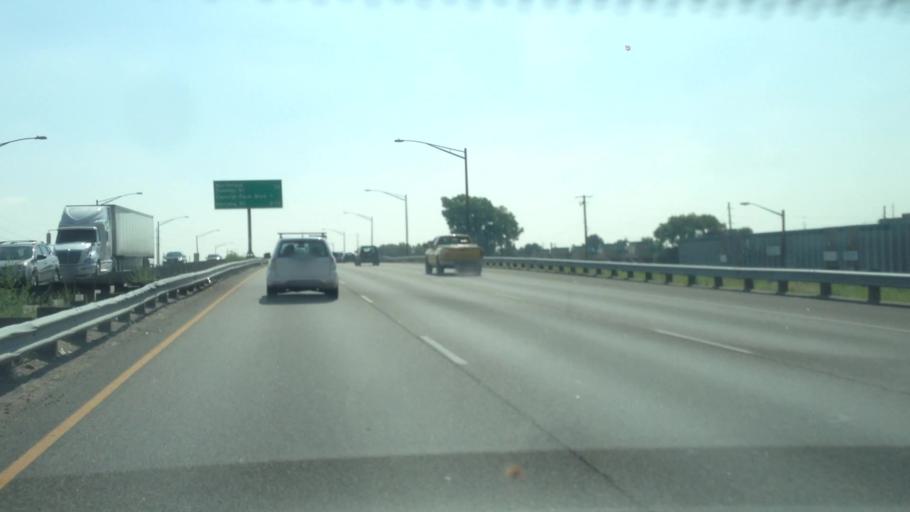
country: US
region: Colorado
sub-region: Adams County
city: Commerce City
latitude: 39.7783
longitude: -104.9147
